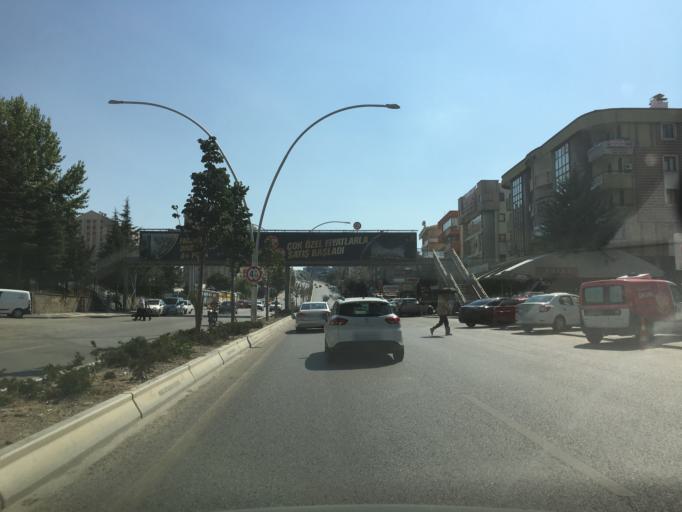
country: TR
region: Ankara
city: Cankaya
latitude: 39.8736
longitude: 32.8622
